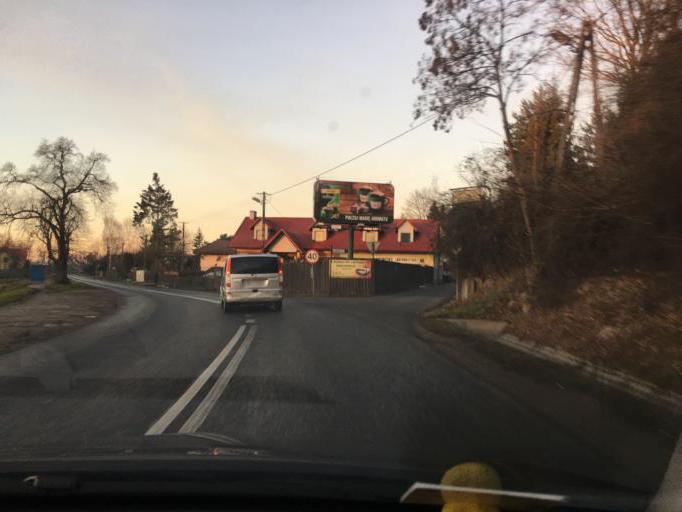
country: PL
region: Lesser Poland Voivodeship
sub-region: Krakow
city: Krakow
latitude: 50.0474
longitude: 19.8847
